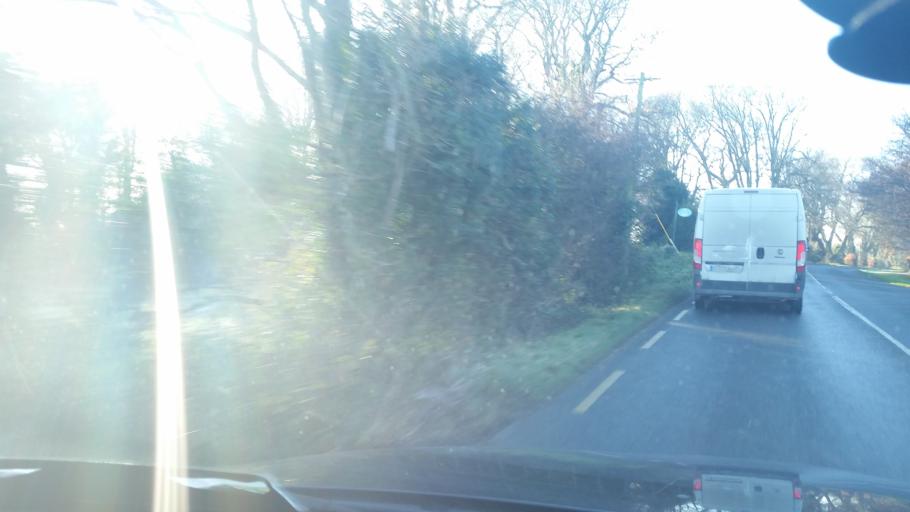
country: IE
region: Leinster
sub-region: Loch Garman
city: Ballinroad
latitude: 52.5331
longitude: -6.3505
